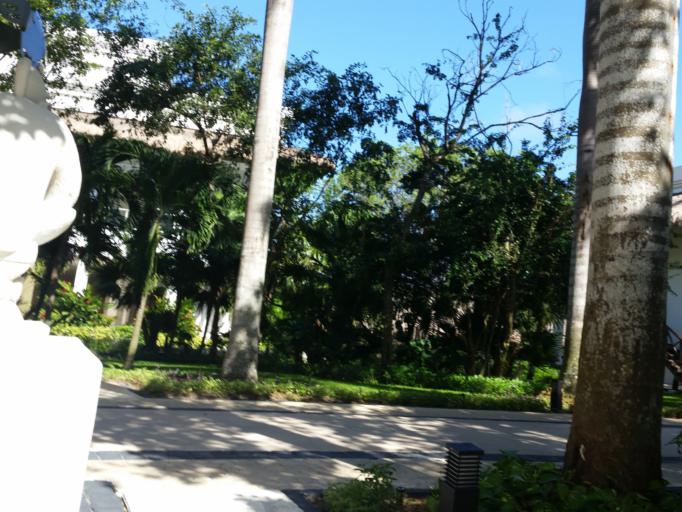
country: MX
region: Quintana Roo
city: Playa del Carmen
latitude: 20.6712
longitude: -87.0336
